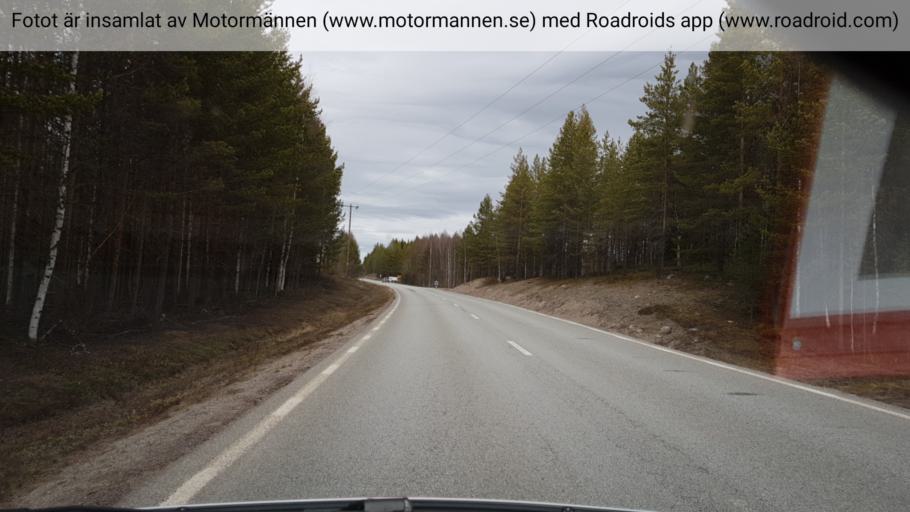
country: SE
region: Vaesterbotten
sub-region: Asele Kommun
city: Asele
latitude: 63.8761
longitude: 17.2022
